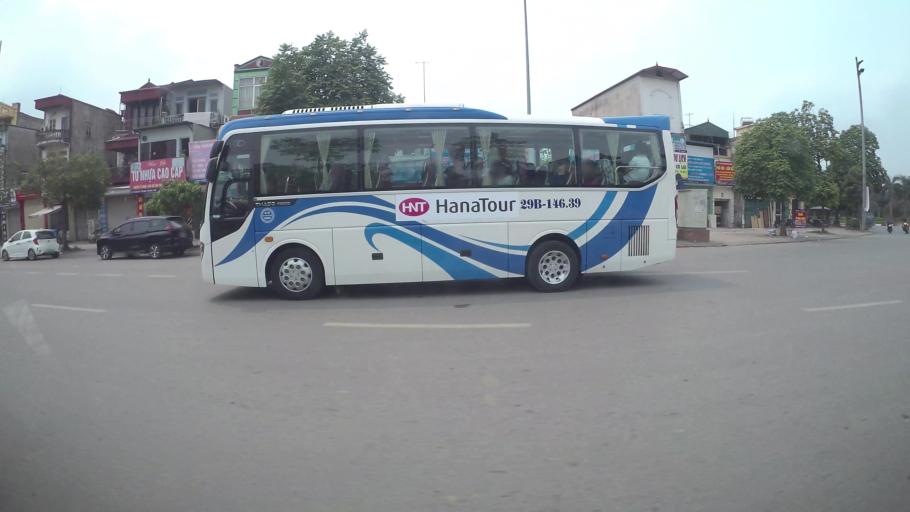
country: VN
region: Ha Noi
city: Trau Quy
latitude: 21.0747
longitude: 105.9070
